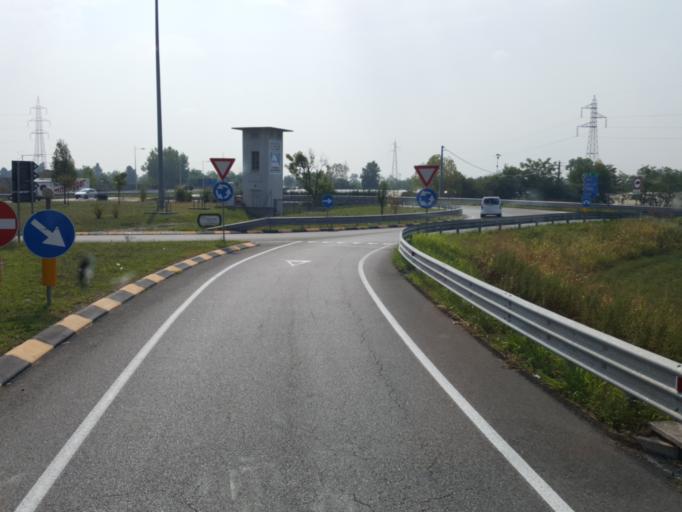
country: IT
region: Lombardy
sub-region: Provincia di Bergamo
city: Bolgare
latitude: 45.6484
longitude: 9.8191
